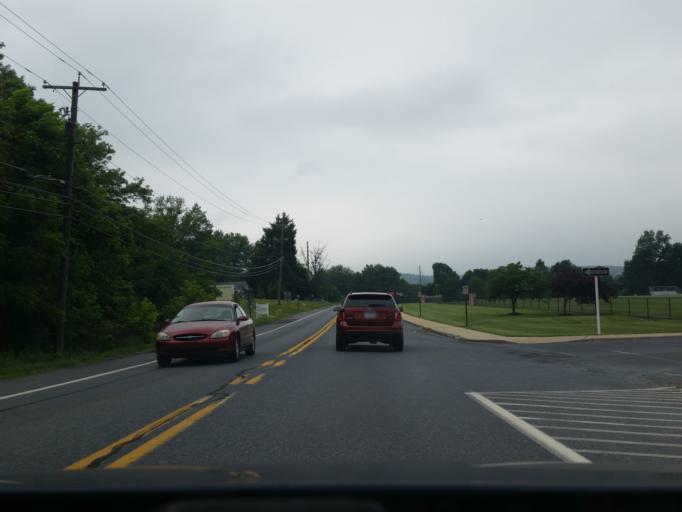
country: US
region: Pennsylvania
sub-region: Lebanon County
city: Annville
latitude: 40.3217
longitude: -76.5104
